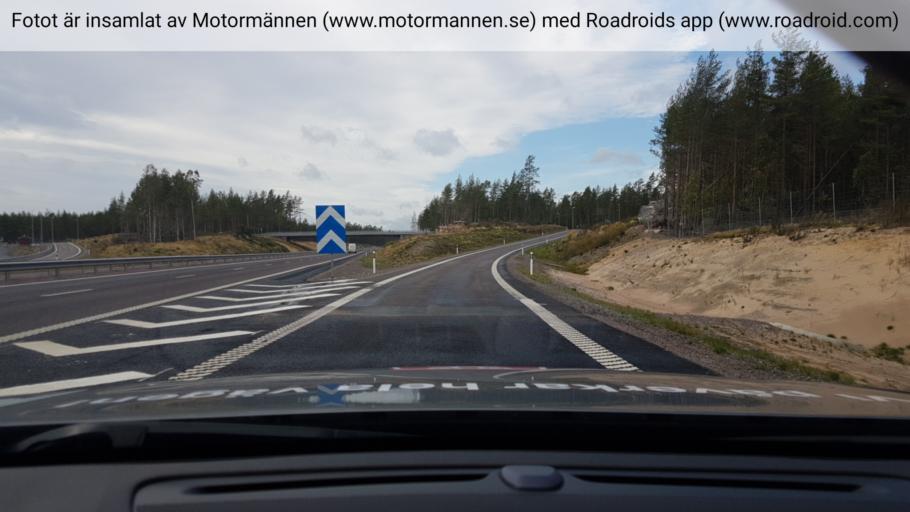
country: SE
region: Vaermland
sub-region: Kils Kommun
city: Kil
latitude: 59.3850
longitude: 13.3412
